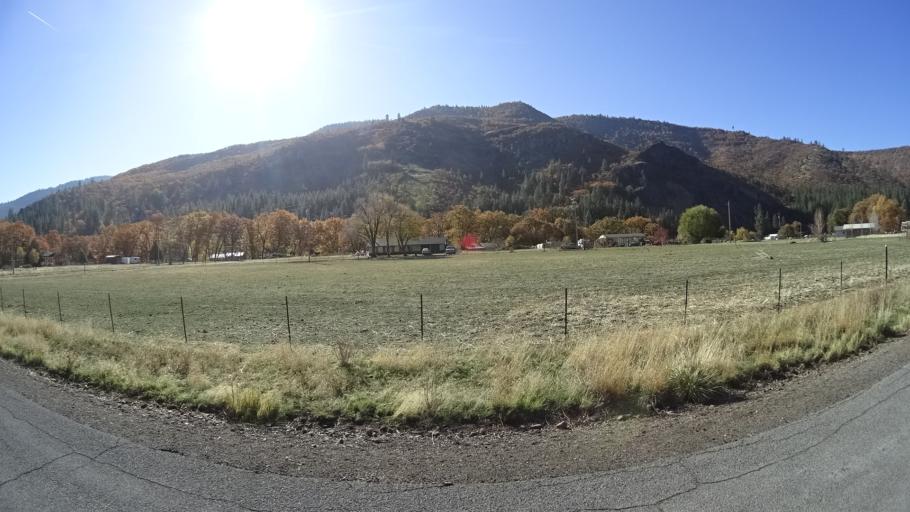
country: US
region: California
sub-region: Siskiyou County
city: Montague
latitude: 41.9670
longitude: -122.2613
